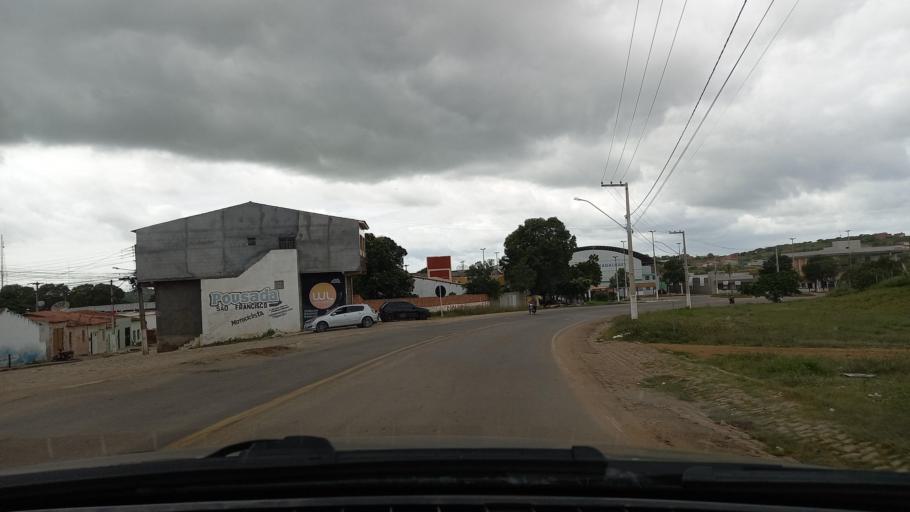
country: BR
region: Sergipe
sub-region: Caninde De Sao Francisco
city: Caninde de Sao Francisco
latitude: -9.6660
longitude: -37.7947
